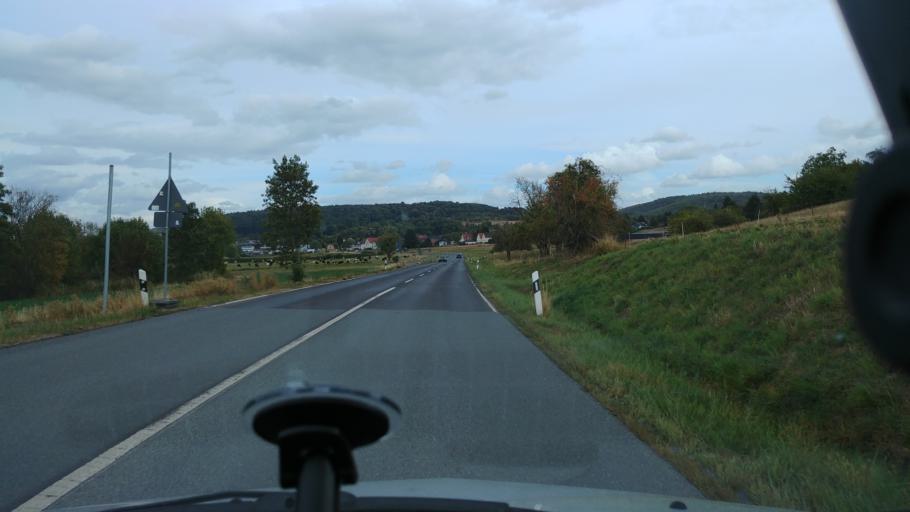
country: DE
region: Hesse
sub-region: Regierungsbezirk Darmstadt
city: Glauburg
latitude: 50.3388
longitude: 9.0214
